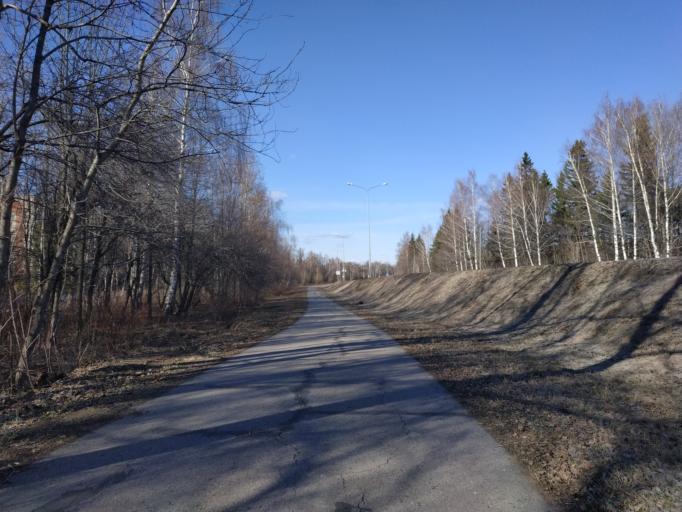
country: RU
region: Chuvashia
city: Ishley
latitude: 56.1217
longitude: 47.0599
